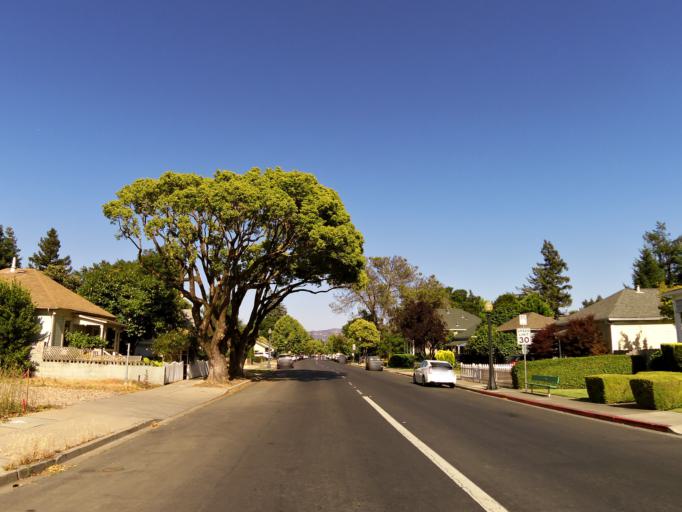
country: US
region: California
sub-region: Napa County
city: Napa
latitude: 38.2972
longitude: -122.3002
